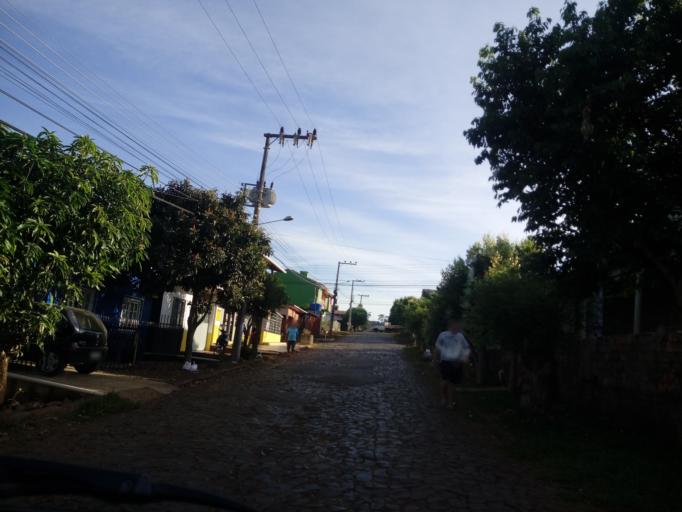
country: BR
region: Santa Catarina
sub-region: Chapeco
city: Chapeco
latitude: -27.0890
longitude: -52.6766
